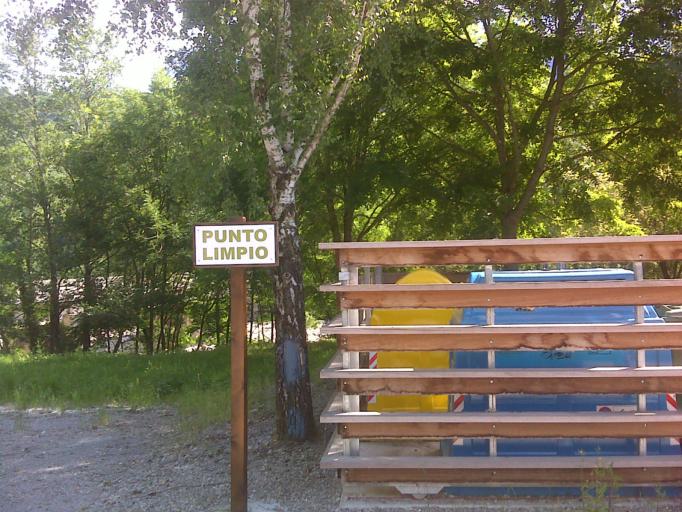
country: ES
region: Cantabria
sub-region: Provincia de Cantabria
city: Santiurde de Toranzo
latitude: 43.1964
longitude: -3.9147
